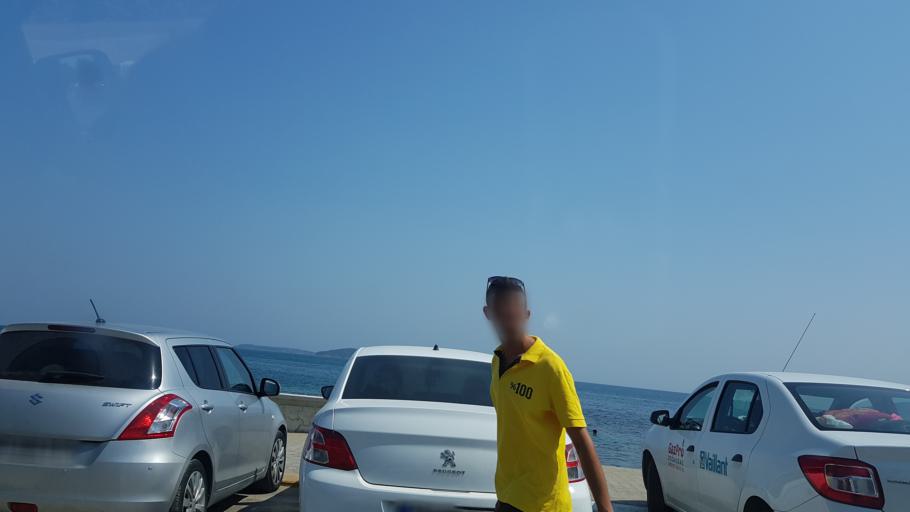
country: TR
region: Izmir
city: Urla
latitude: 38.3729
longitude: 26.7620
